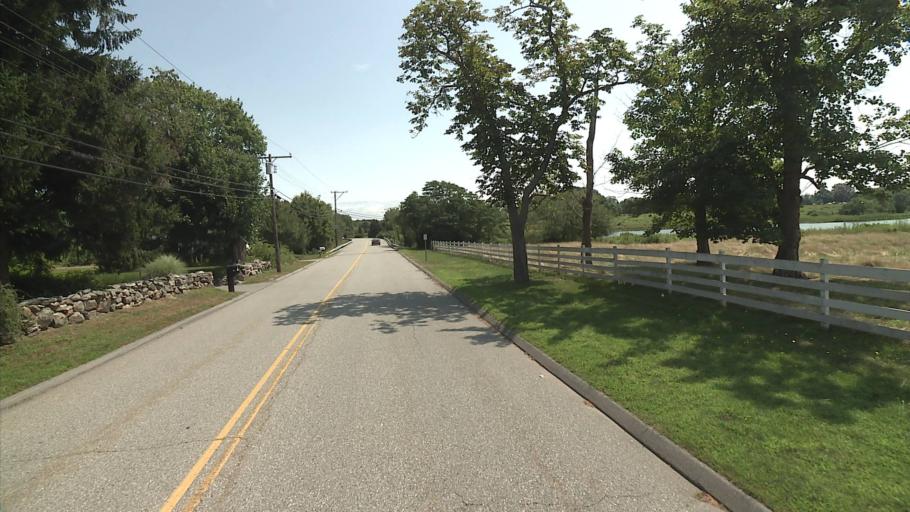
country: US
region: Connecticut
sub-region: New London County
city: Central Waterford
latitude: 41.3066
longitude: -72.1198
